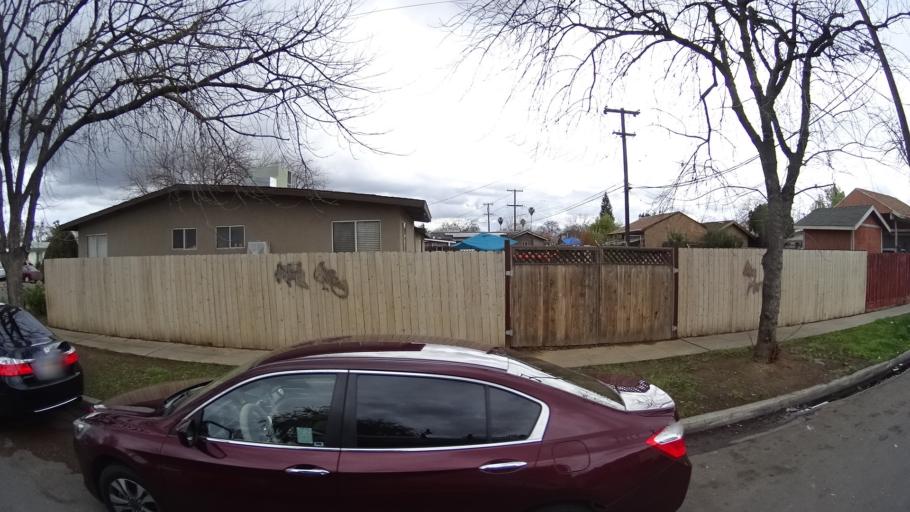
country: US
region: California
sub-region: Fresno County
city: West Park
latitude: 36.7818
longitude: -119.8399
